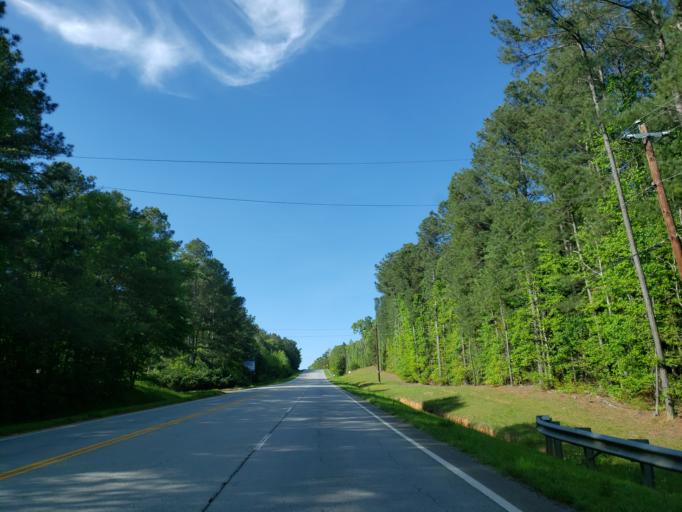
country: US
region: Georgia
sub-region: Haralson County
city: Tallapoosa
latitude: 33.7183
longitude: -85.2808
